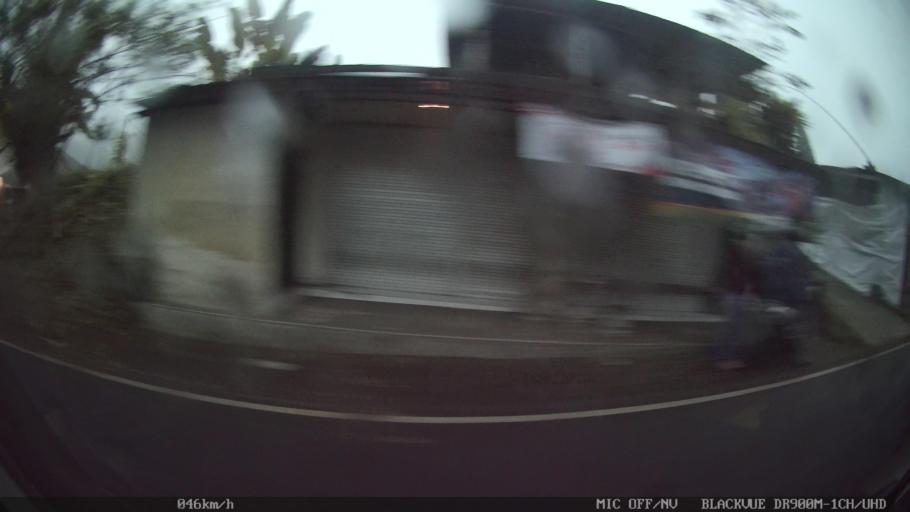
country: ID
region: Bali
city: Banjar Taro Kelod
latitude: -8.3424
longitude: 115.2807
